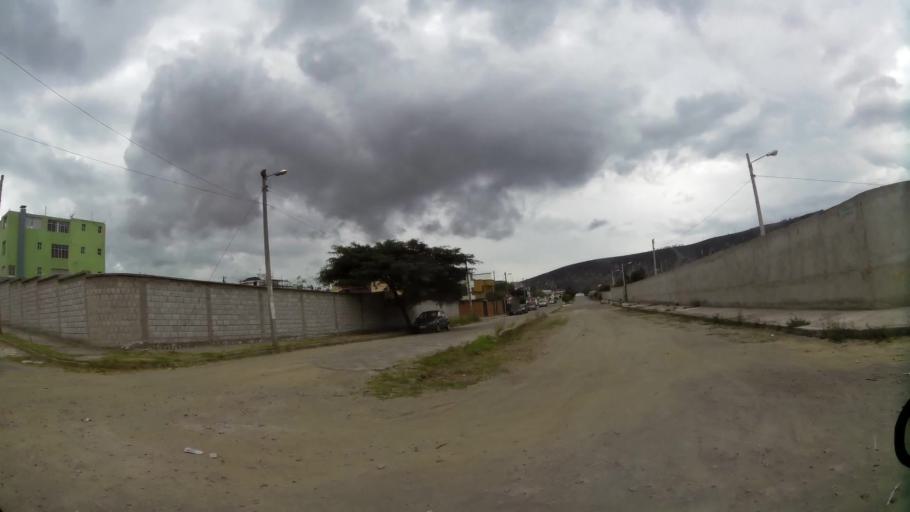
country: EC
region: Pichincha
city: Quito
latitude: -0.0083
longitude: -78.4573
